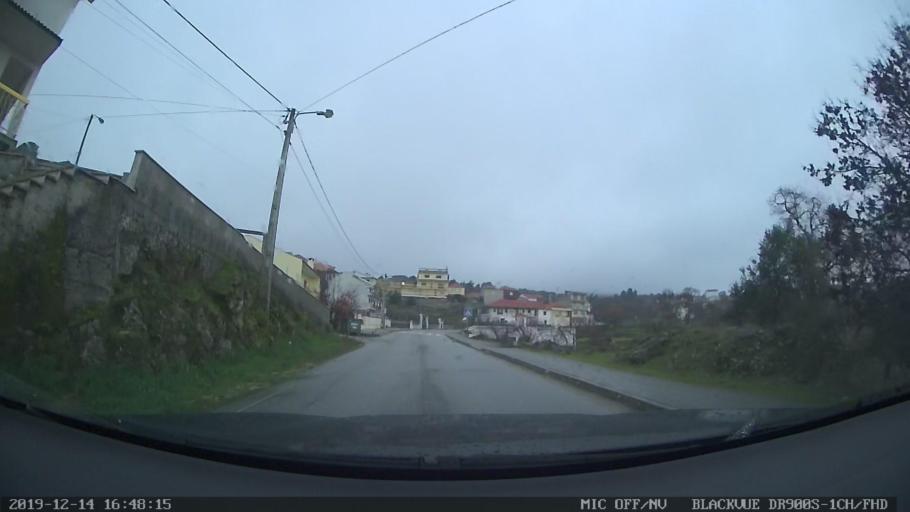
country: PT
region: Vila Real
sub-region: Murca
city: Murca
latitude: 41.4046
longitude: -7.5012
